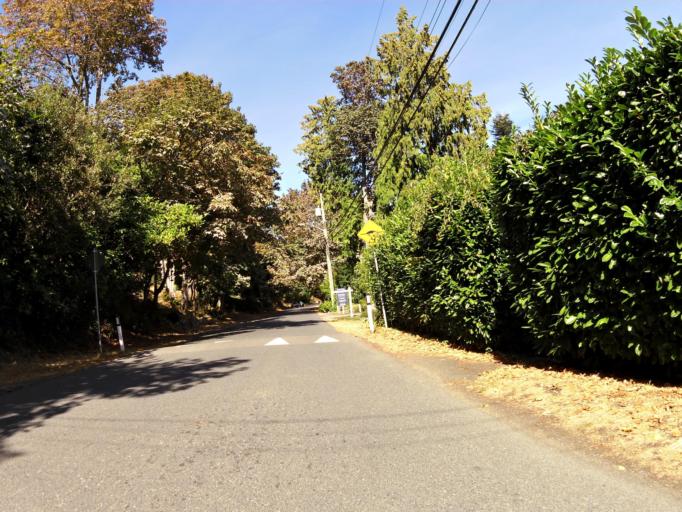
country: CA
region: British Columbia
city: Victoria
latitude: 48.5208
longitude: -123.3710
